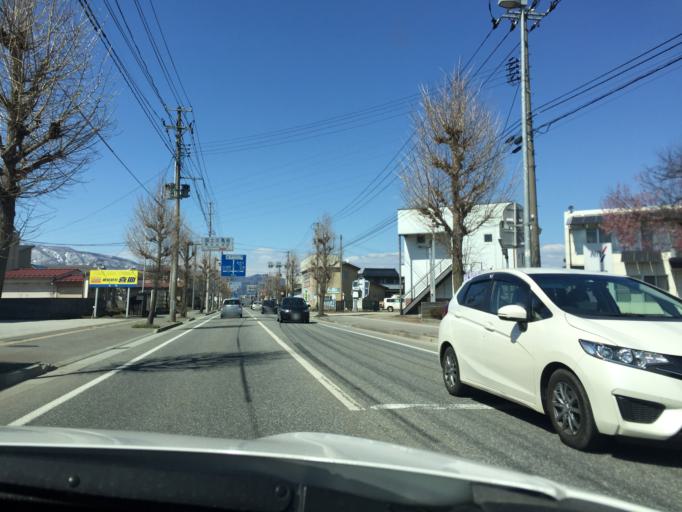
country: JP
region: Yamagata
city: Nagai
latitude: 38.1098
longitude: 140.0431
